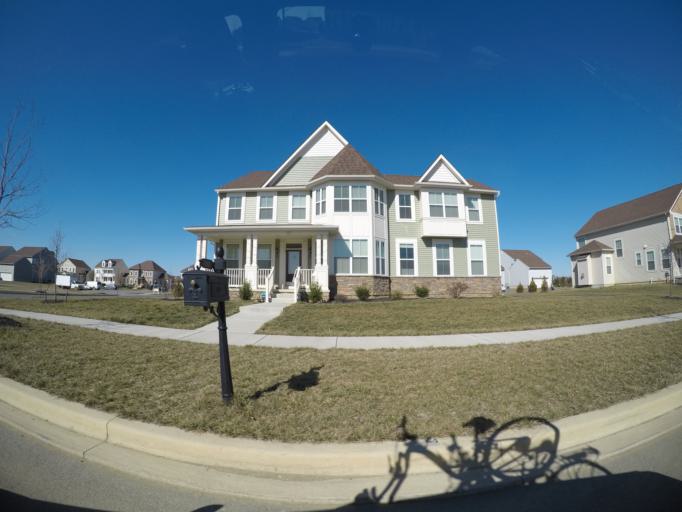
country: US
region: Delaware
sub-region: New Castle County
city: Middletown
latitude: 39.5098
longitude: -75.6656
